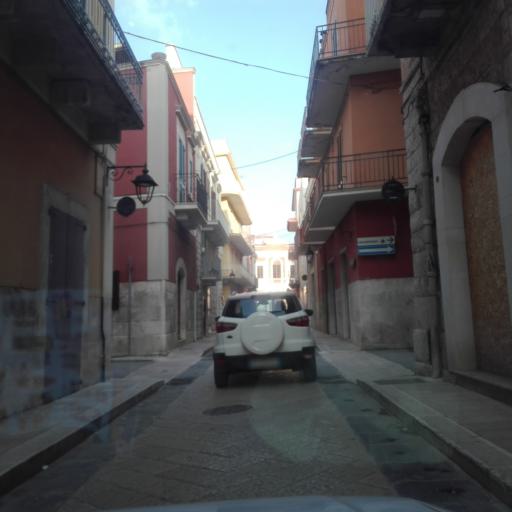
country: IT
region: Apulia
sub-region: Provincia di Bari
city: Corato
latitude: 41.1546
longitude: 16.4121
